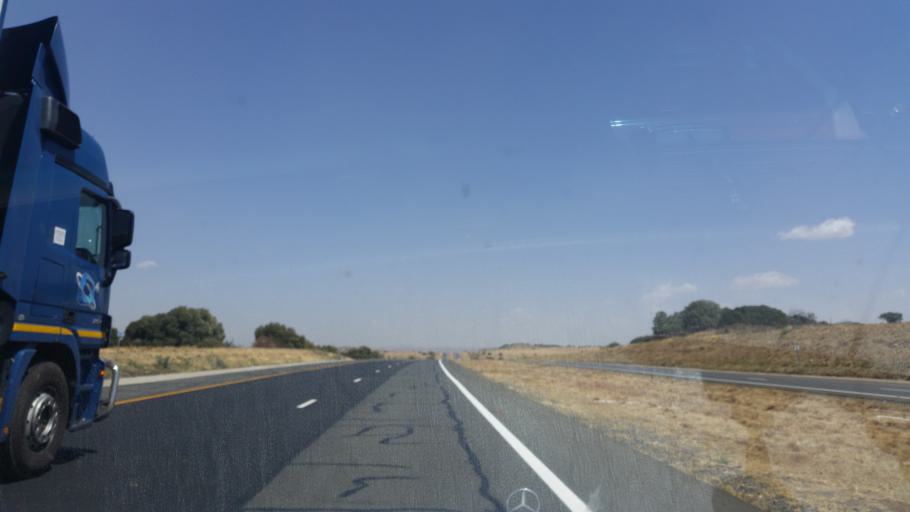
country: ZA
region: Orange Free State
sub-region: Lejweleputswa District Municipality
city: Brandfort
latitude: -28.9084
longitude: 26.4596
